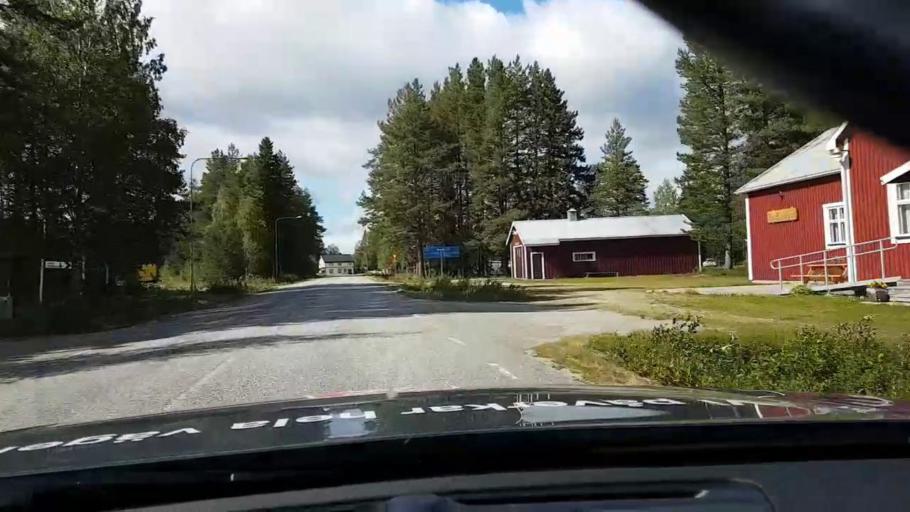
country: SE
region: Vaesterbotten
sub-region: Asele Kommun
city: Asele
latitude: 63.9368
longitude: 17.2856
